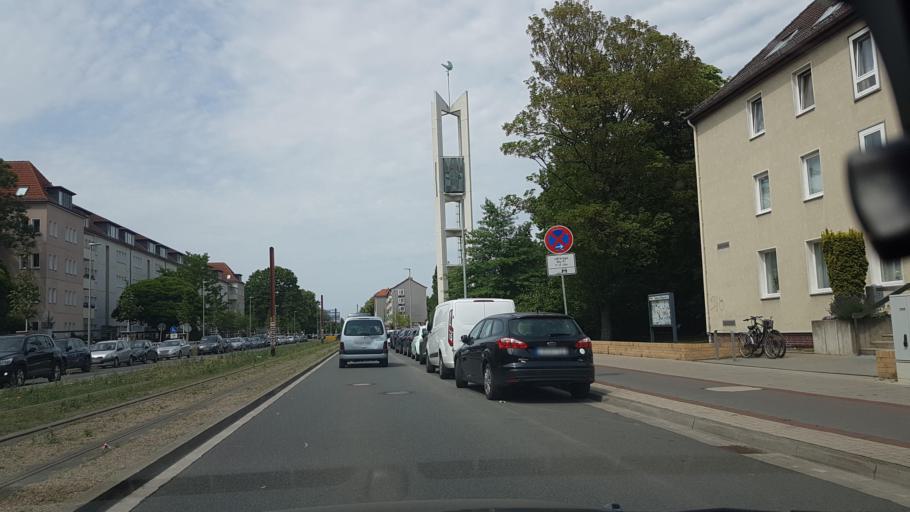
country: DE
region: Lower Saxony
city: Hemmingen
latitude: 52.3402
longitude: 9.7174
